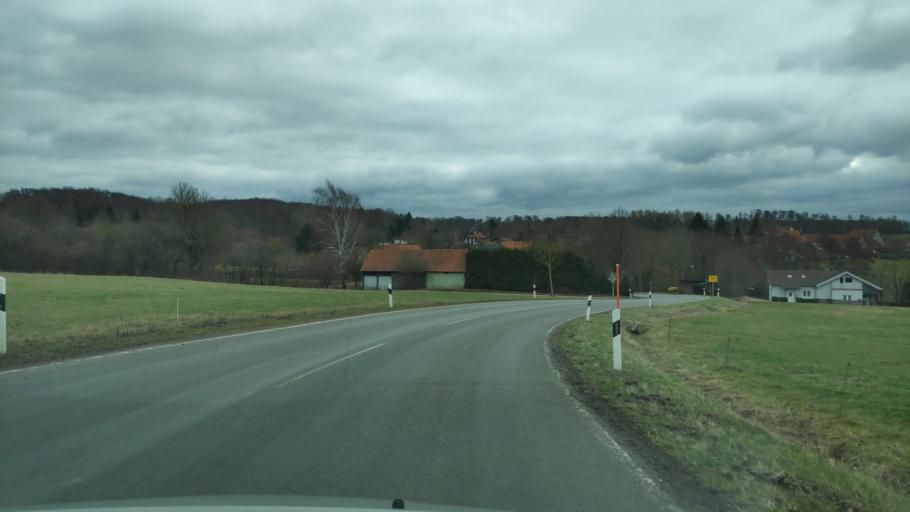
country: DE
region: Lower Saxony
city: Hessisch Oldendorf
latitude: 52.2153
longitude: 9.2913
